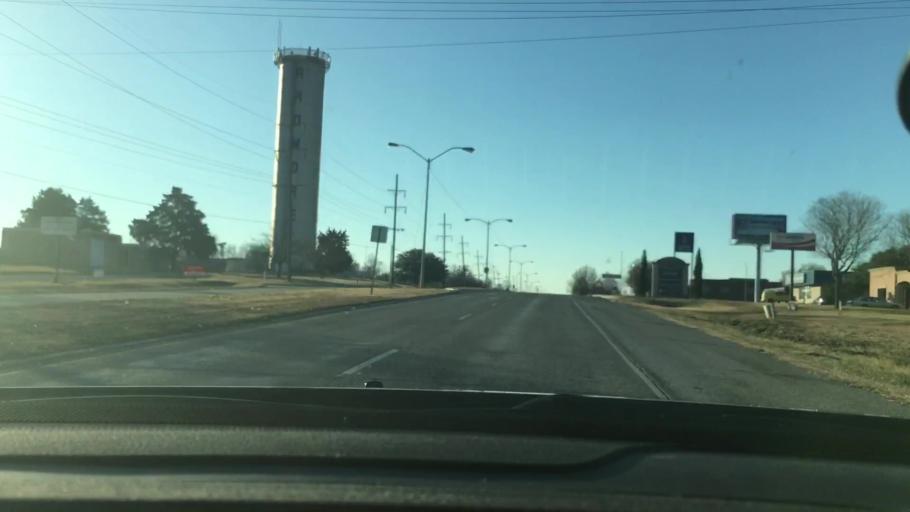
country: US
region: Oklahoma
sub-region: Carter County
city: Ardmore
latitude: 34.1997
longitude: -97.1432
